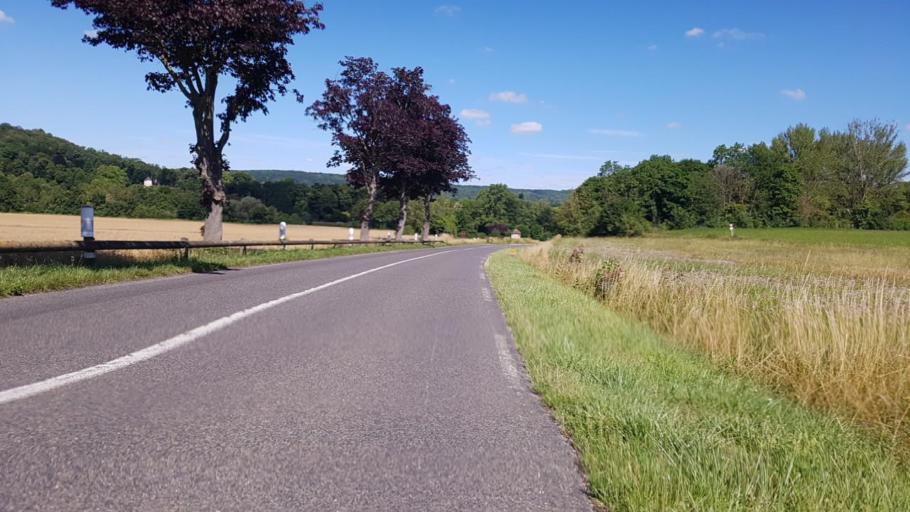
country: FR
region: Ile-de-France
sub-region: Departement de Seine-et-Marne
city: Saacy-sur-Marne
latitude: 48.9677
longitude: 3.1955
